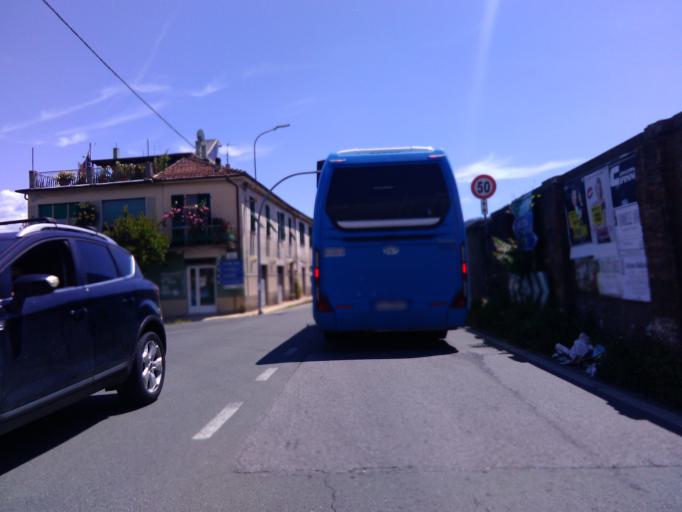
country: IT
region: Tuscany
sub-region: Provincia di Massa-Carrara
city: Terrarossa
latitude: 44.2234
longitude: 9.9697
